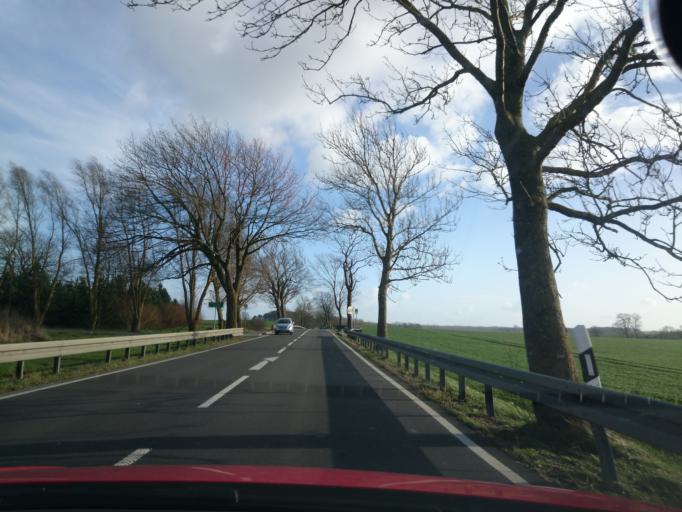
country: DE
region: Mecklenburg-Vorpommern
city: Barth
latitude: 54.3070
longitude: 12.7178
